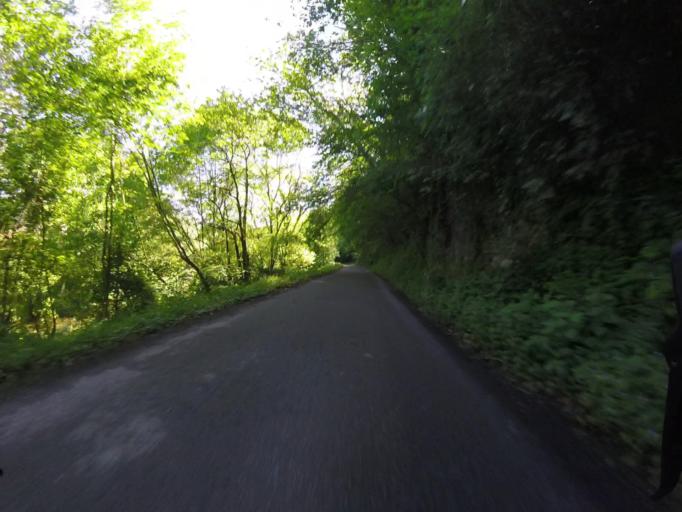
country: ES
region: Navarre
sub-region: Provincia de Navarra
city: Bera
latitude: 43.2750
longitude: -1.6995
